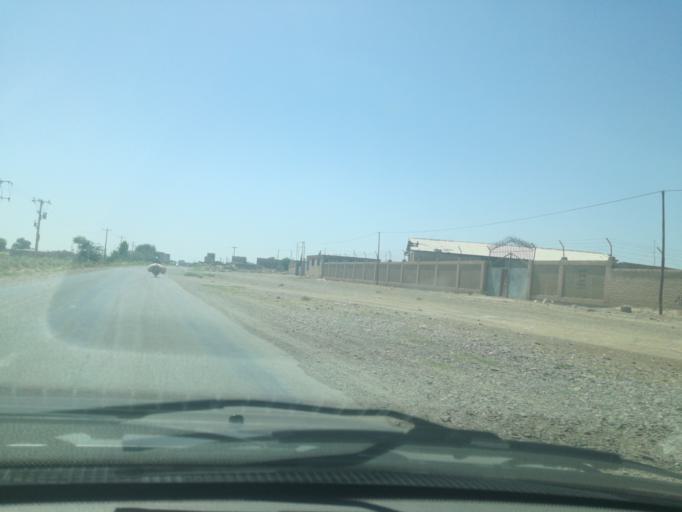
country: IR
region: Razavi Khorasan
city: Sarakhs
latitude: 36.5628
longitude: 61.1464
